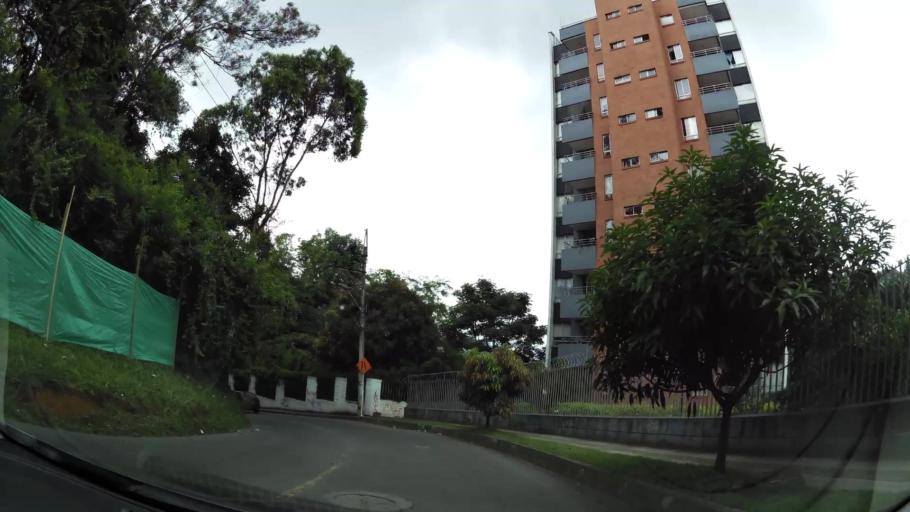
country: CO
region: Antioquia
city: Medellin
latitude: 6.2748
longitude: -75.5830
